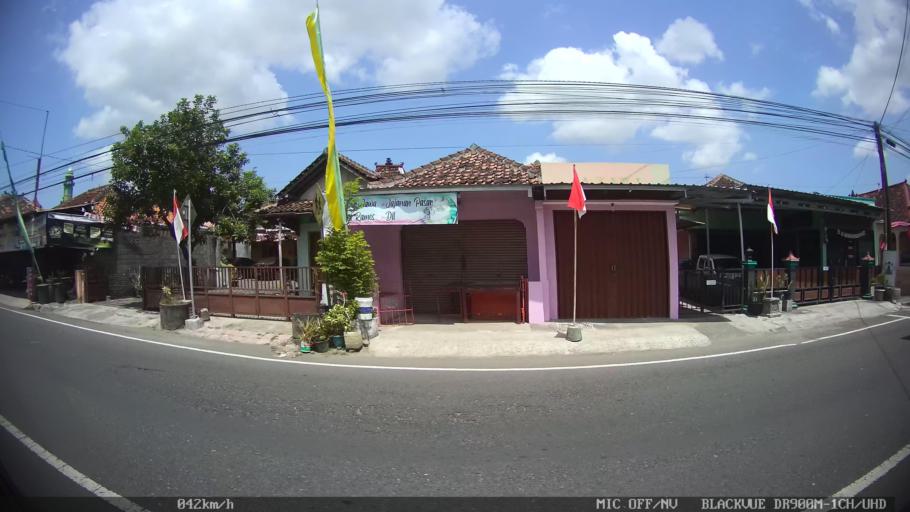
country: ID
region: Daerah Istimewa Yogyakarta
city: Bantul
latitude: -7.8925
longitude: 110.3319
